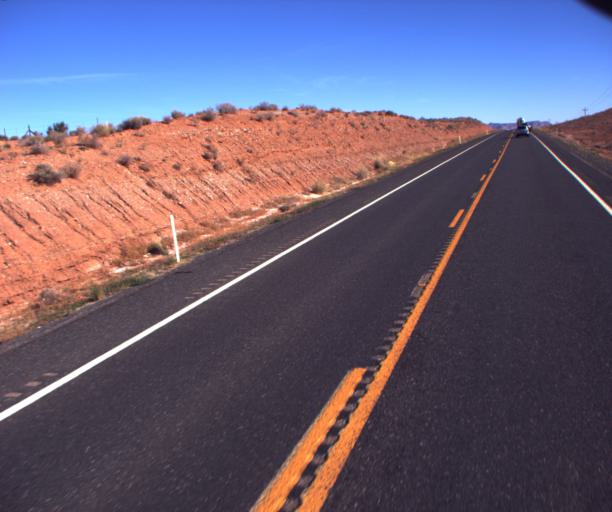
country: US
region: Arizona
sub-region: Coconino County
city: Fredonia
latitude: 36.9029
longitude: -112.5967
